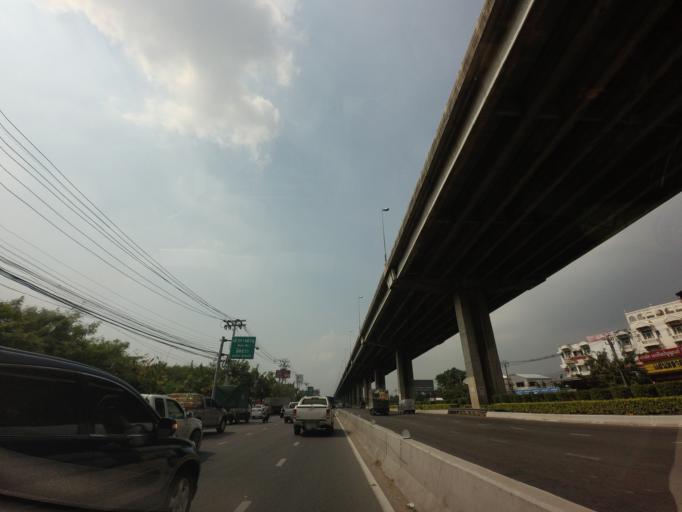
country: TH
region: Bangkok
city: Taling Chan
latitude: 13.7833
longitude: 100.4047
